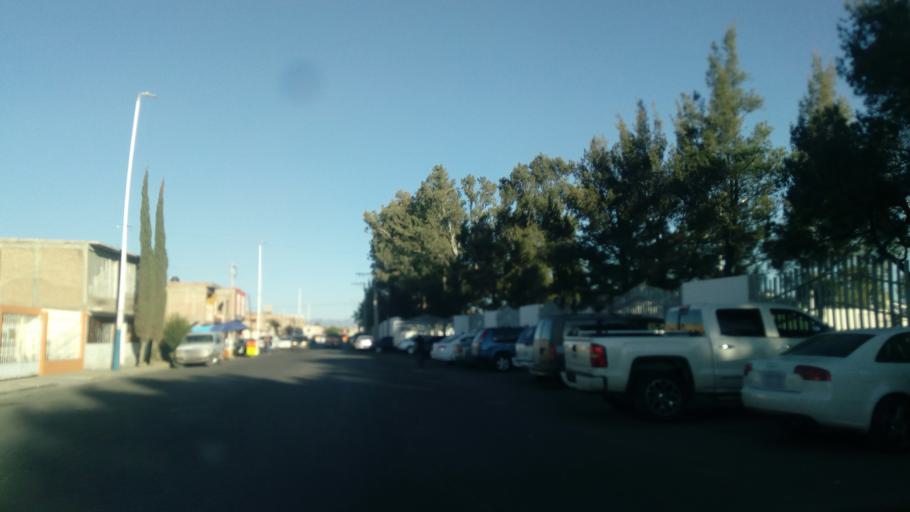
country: MX
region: Durango
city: Victoria de Durango
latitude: 23.9978
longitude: -104.6779
